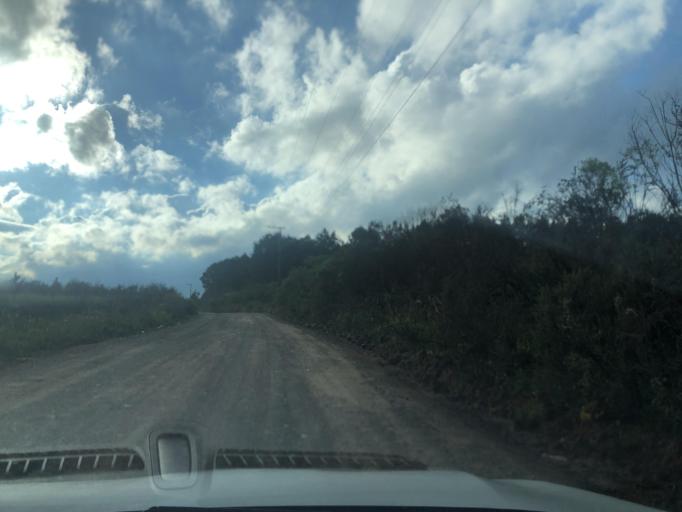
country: BR
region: Santa Catarina
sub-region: Lages
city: Lages
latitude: -27.7918
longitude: -50.3182
